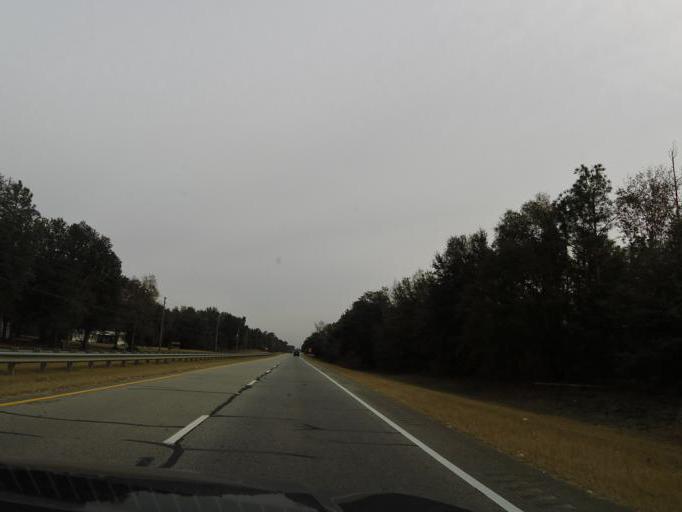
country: US
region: Georgia
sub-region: Decatur County
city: Bainbridge
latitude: 30.9322
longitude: -84.6418
